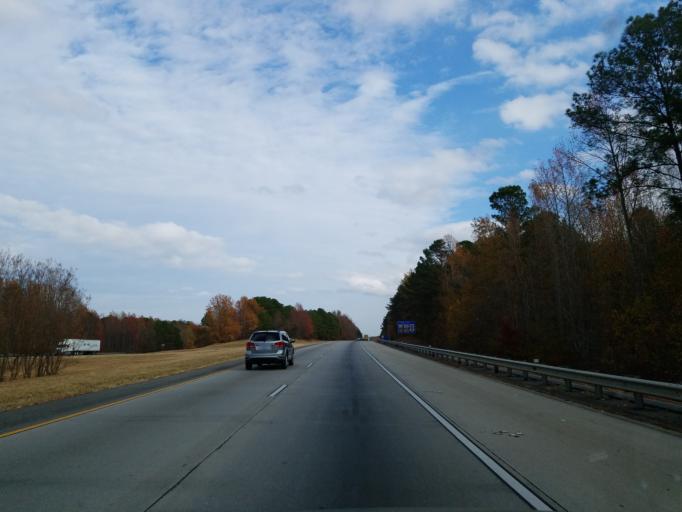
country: US
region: Georgia
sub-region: Haralson County
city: Tallapoosa
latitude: 33.6813
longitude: -85.2958
